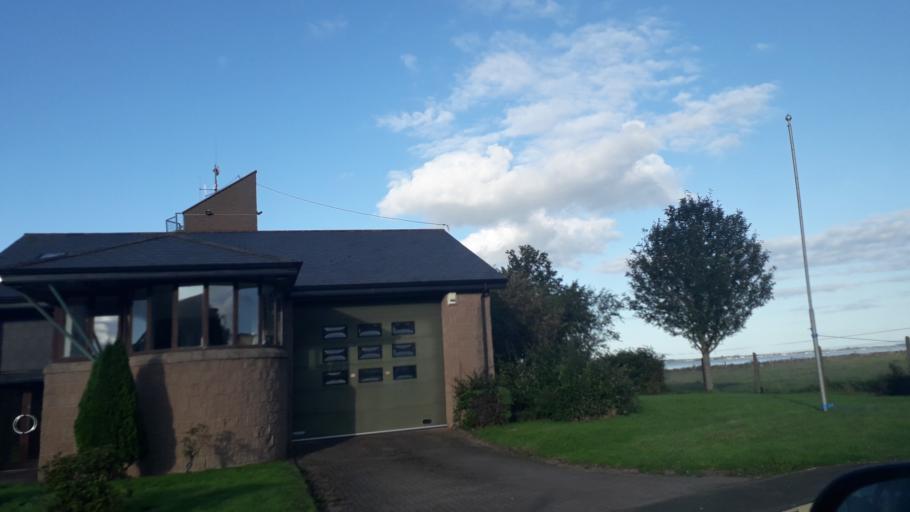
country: IE
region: Leinster
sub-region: Lu
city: Carlingford
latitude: 54.0383
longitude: -6.1756
